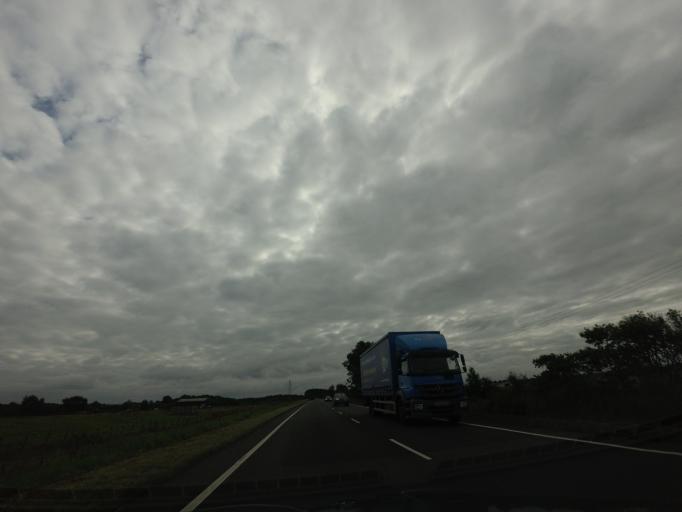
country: GB
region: Scotland
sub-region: Dumfries and Galloway
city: Annan
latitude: 54.9921
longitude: -3.1662
